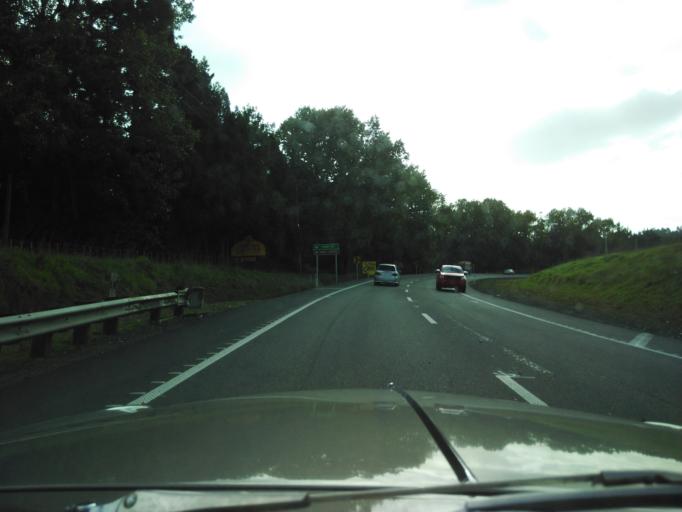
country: NZ
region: Auckland
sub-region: Auckland
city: Warkworth
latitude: -36.4381
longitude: 174.6480
